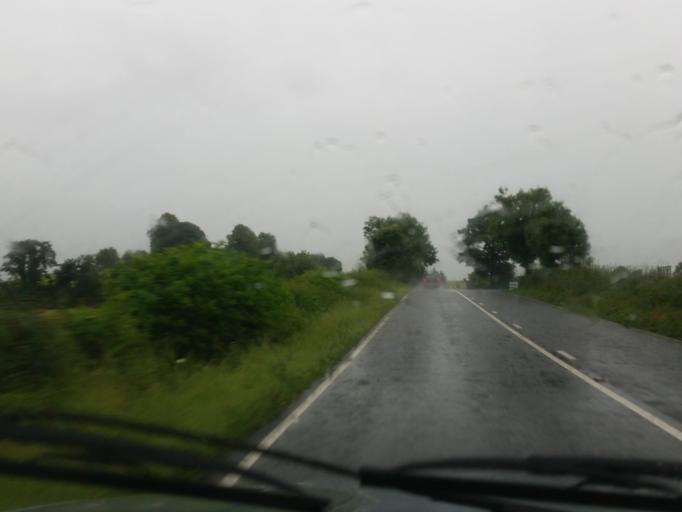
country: GB
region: Northern Ireland
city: Lisnaskea
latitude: 54.2788
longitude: -7.4670
